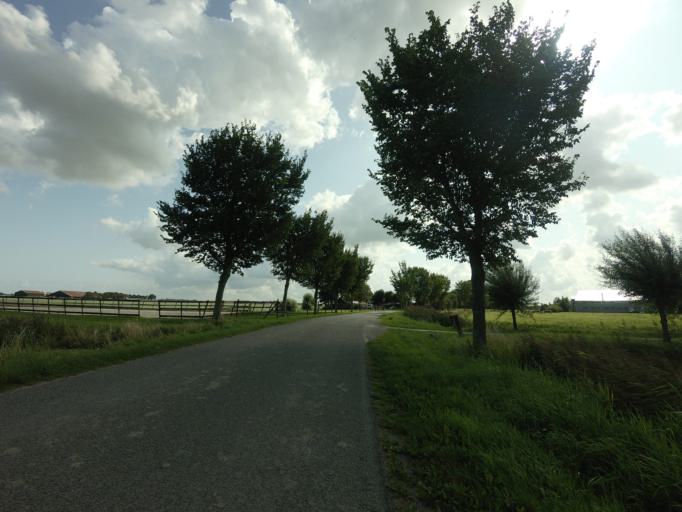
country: NL
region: Friesland
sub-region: Gemeente Het Bildt
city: Minnertsga
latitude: 53.2586
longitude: 5.5995
